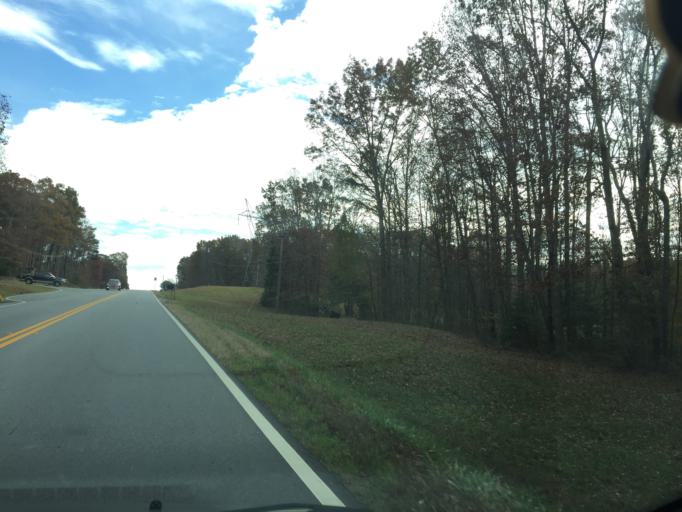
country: US
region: Georgia
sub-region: Dade County
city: Trenton
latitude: 34.8160
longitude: -85.4906
